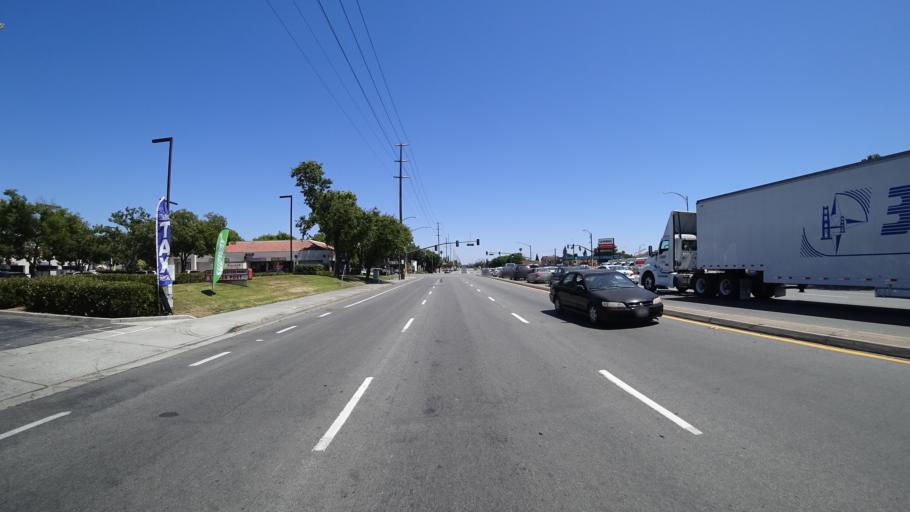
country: US
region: California
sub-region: Santa Clara County
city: Seven Trees
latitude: 37.3087
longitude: -121.8482
